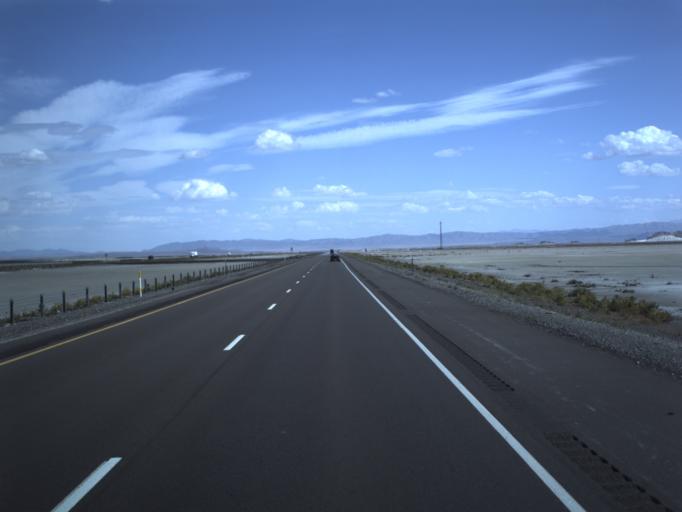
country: US
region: Utah
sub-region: Tooele County
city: Wendover
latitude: 40.7279
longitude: -113.3627
